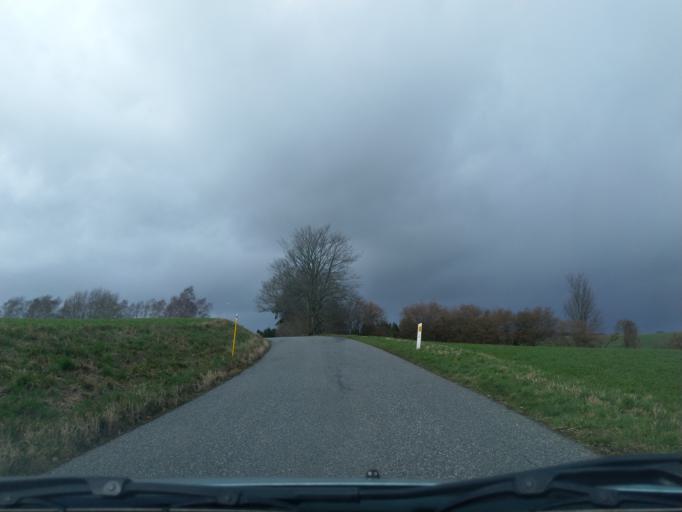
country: DK
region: Zealand
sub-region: Naestved Kommune
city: Fuglebjerg
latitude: 55.3398
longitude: 11.5869
